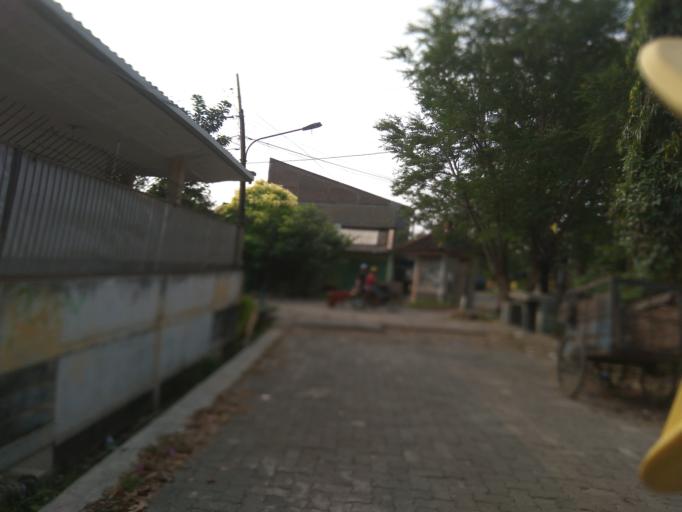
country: ID
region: Central Java
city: Semarang
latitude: -6.9734
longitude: 110.3929
